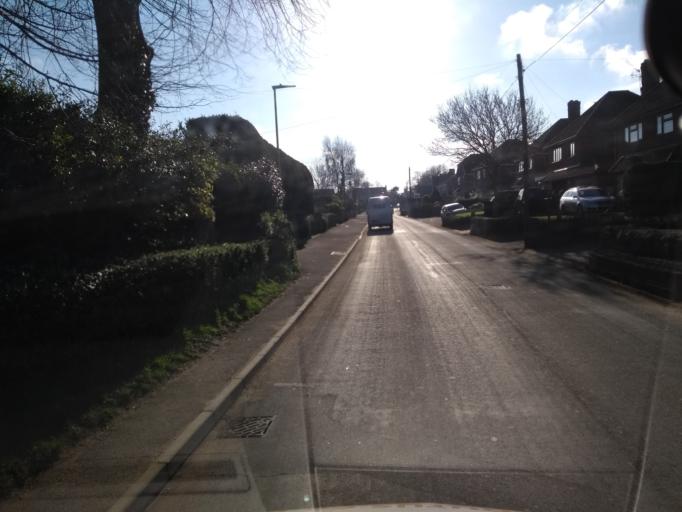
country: GB
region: England
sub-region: Somerset
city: South Petherton
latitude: 50.9465
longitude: -2.8041
